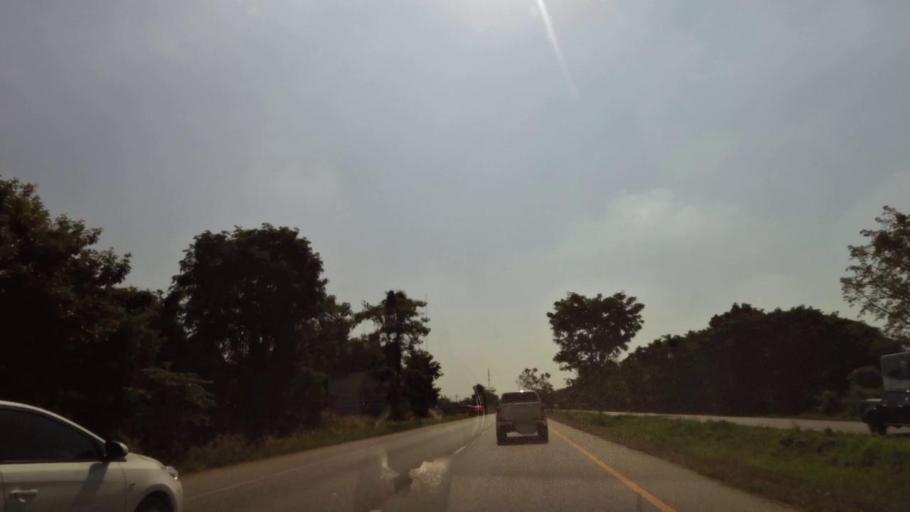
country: TH
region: Phichit
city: Wachira Barami
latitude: 16.4194
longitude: 100.1439
